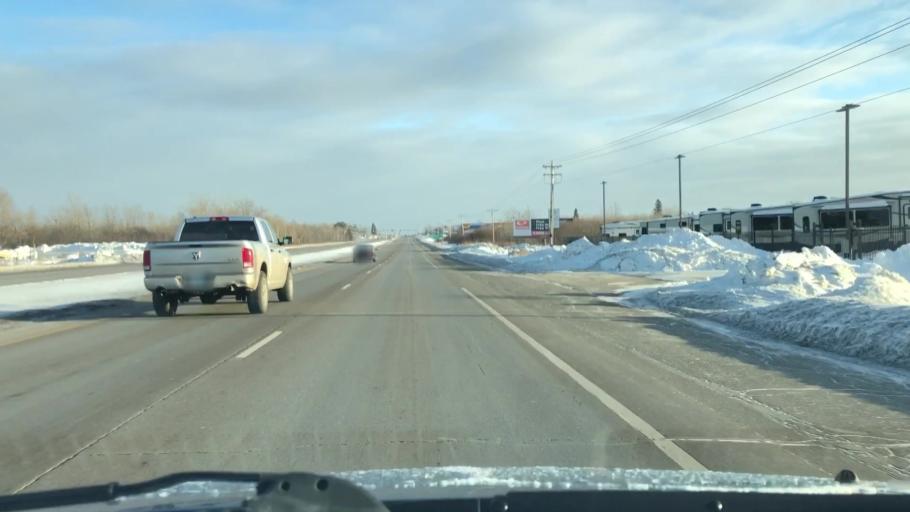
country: US
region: Minnesota
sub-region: Saint Louis County
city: Hermantown
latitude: 46.8320
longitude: -92.2031
